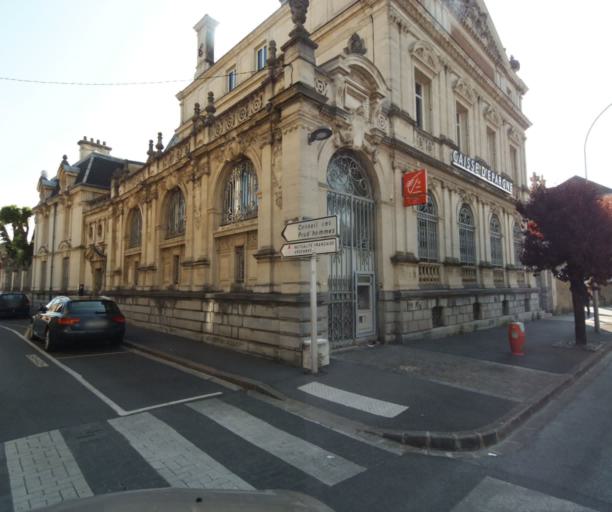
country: FR
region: Champagne-Ardenne
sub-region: Departement des Ardennes
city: Charleville-Mezieres
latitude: 49.7699
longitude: 4.7229
